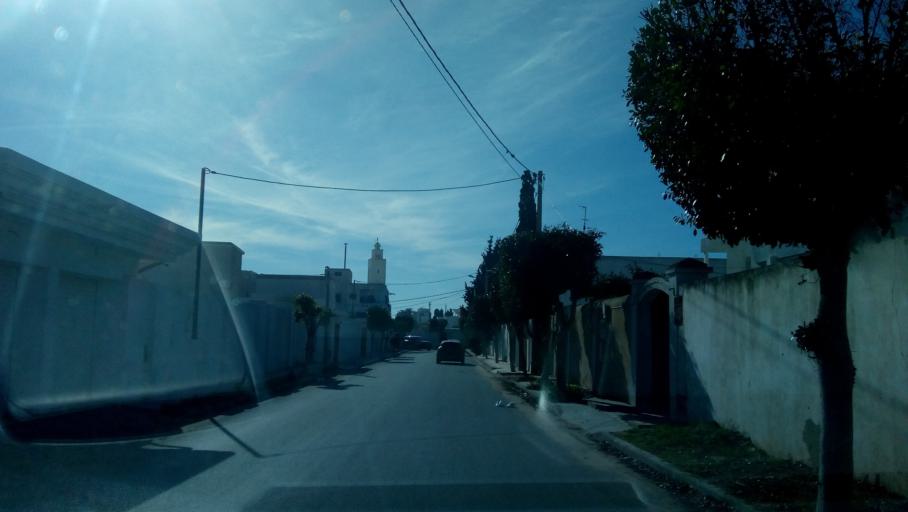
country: TN
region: Safaqis
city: Sfax
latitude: 34.7494
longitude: 10.7386
